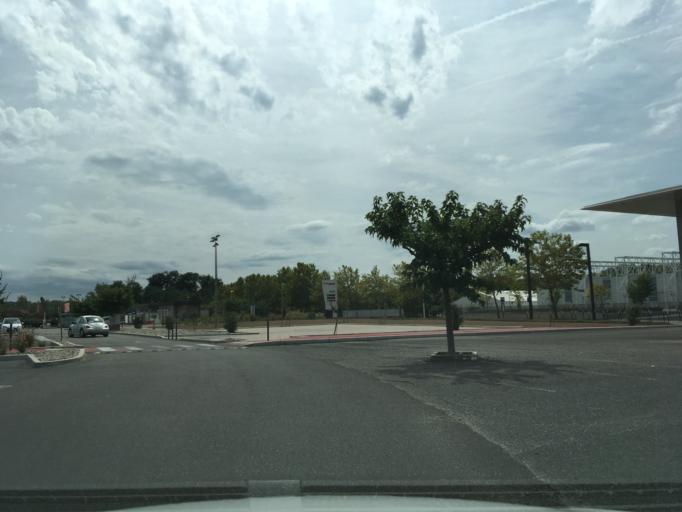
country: FR
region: Aquitaine
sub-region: Departement du Lot-et-Garonne
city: Agen
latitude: 44.1821
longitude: 0.6184
